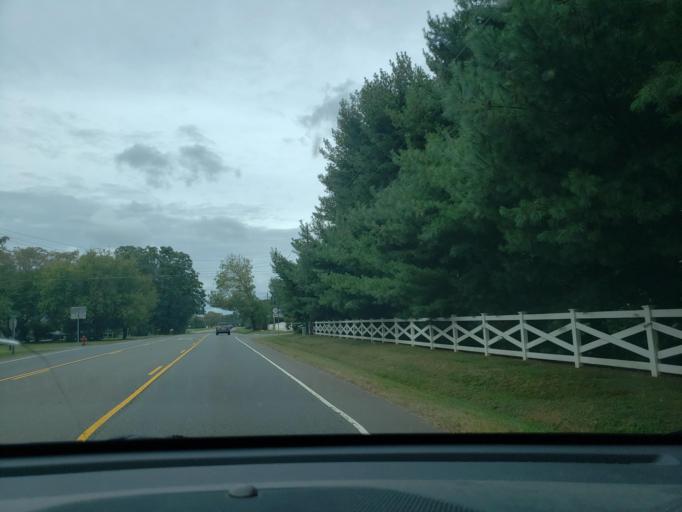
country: US
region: Virginia
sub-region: City of Fredericksburg
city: Fredericksburg
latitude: 38.2574
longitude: -77.4308
